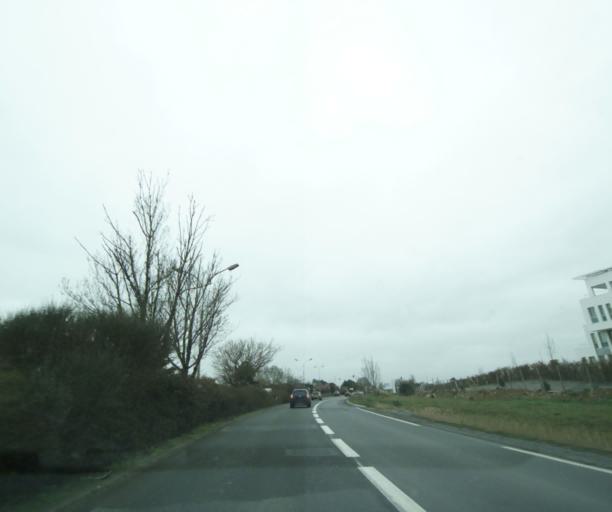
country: FR
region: Poitou-Charentes
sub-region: Departement de la Charente-Maritime
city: Lagord
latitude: 46.1847
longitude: -1.1520
